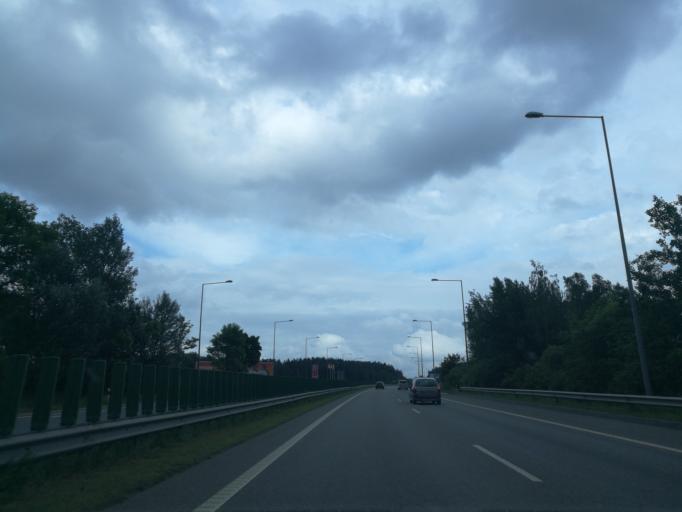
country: LT
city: Grigiskes
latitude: 54.6876
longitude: 25.0502
